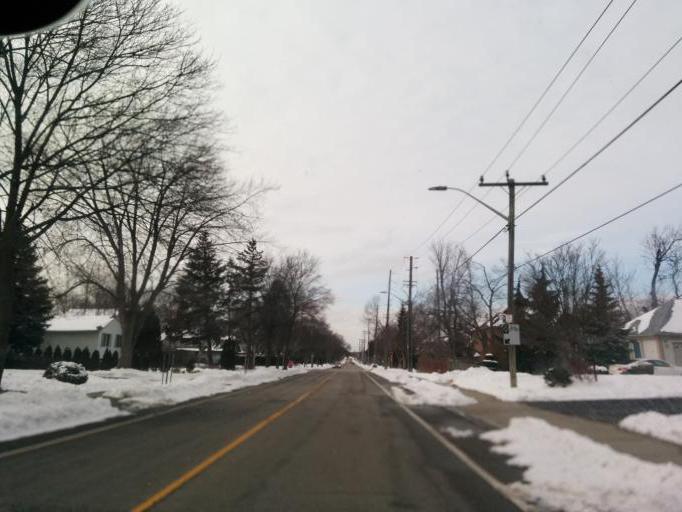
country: CA
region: Ontario
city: Mississauga
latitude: 43.5326
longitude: -79.6633
